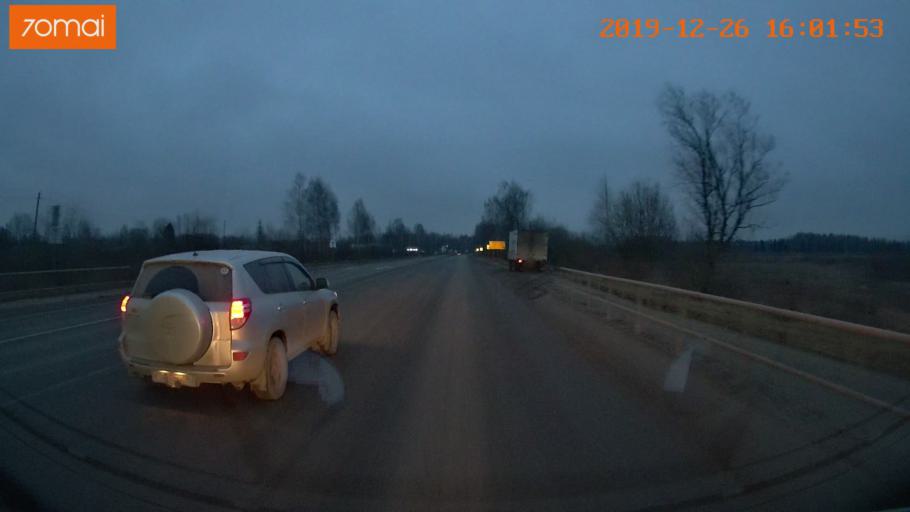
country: RU
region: Jaroslavl
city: Rybinsk
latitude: 58.0152
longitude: 38.8237
